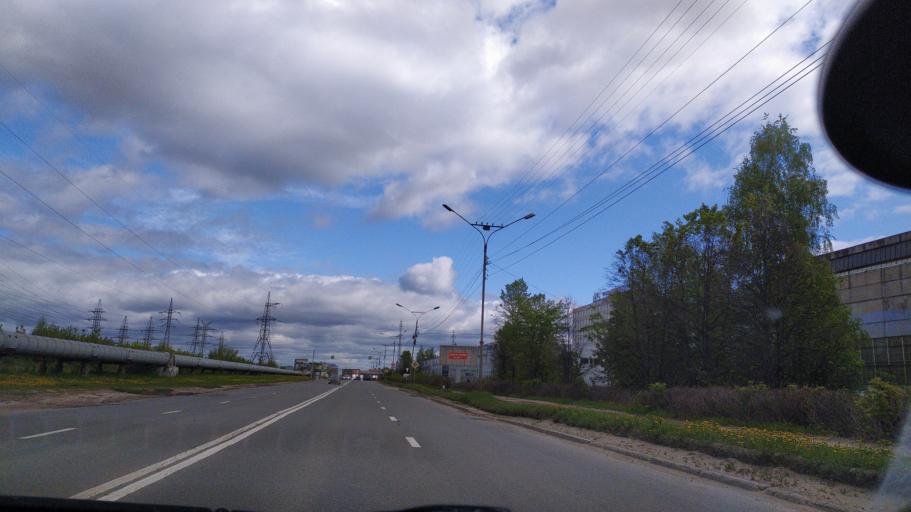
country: RU
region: Chuvashia
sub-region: Cheboksarskiy Rayon
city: Cheboksary
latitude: 56.1242
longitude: 47.3066
